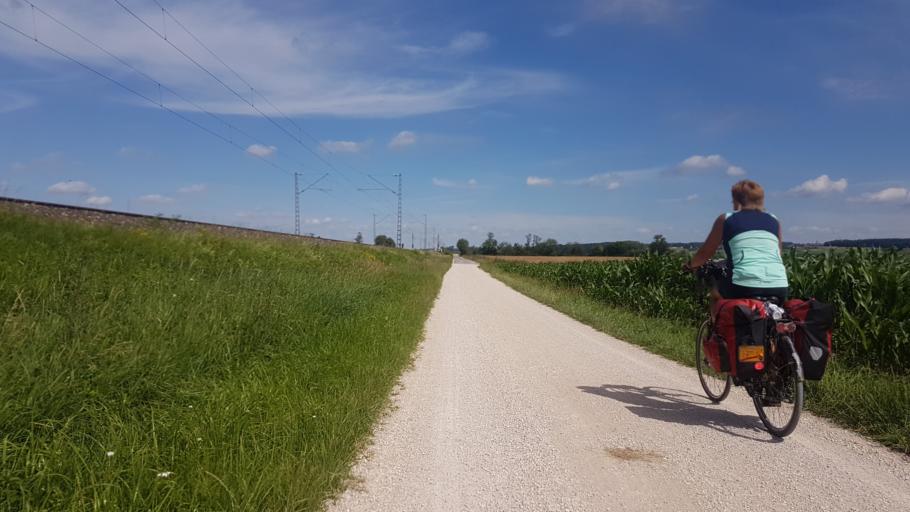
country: DE
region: Bavaria
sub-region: Regierungsbezirk Mittelfranken
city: Markt Berolzheim
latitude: 49.0285
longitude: 10.8447
